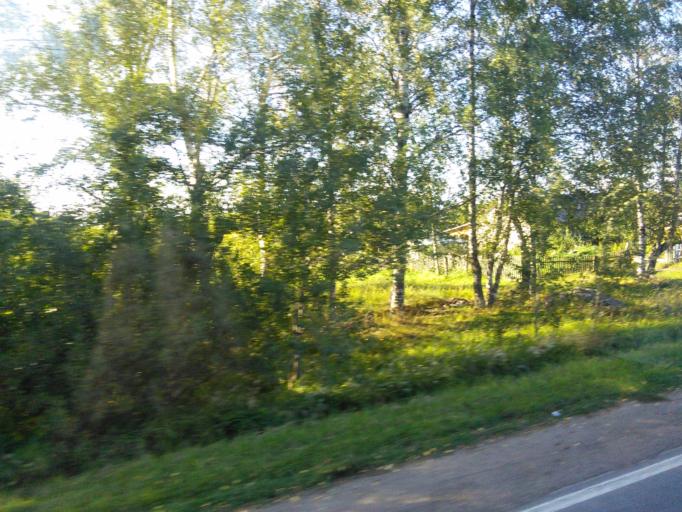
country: RU
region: Jaroslavl
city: Rybinsk
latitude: 58.2857
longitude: 38.8651
